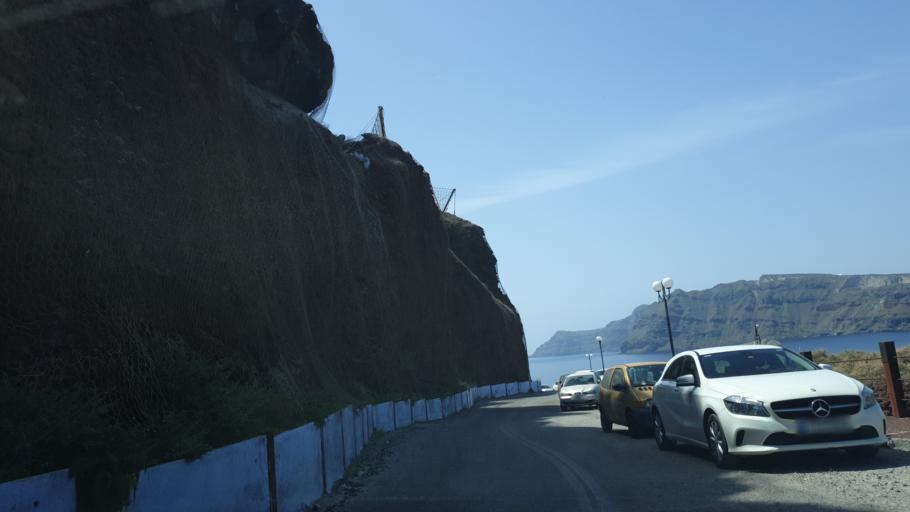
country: GR
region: South Aegean
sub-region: Nomos Kykladon
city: Oia
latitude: 36.4627
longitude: 25.3699
